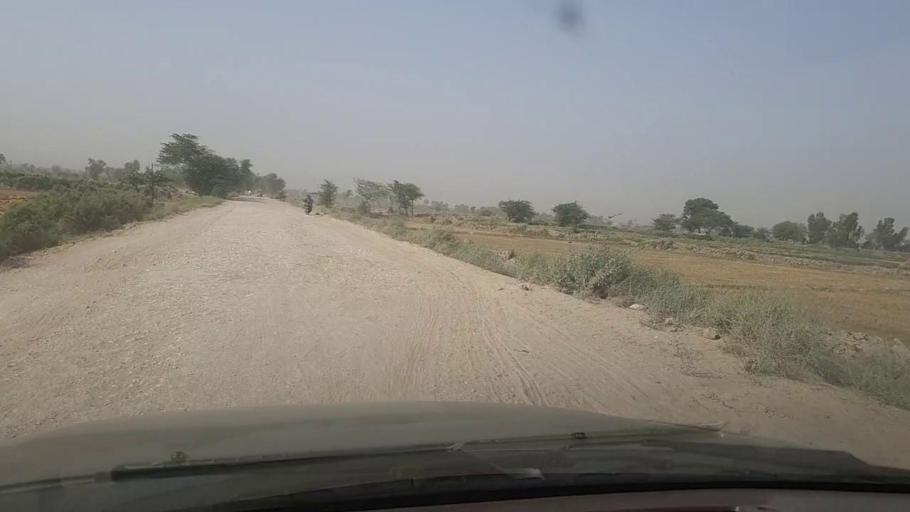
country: PK
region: Sindh
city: Shikarpur
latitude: 27.9280
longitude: 68.6159
